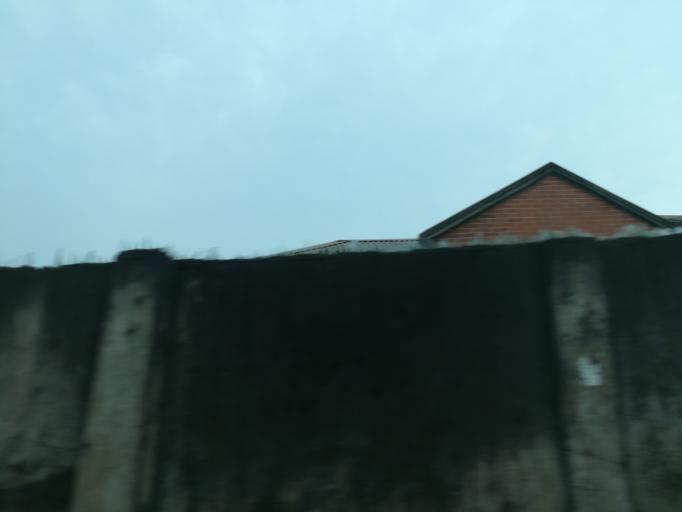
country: NG
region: Rivers
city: Port Harcourt
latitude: 4.8226
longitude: 7.0266
